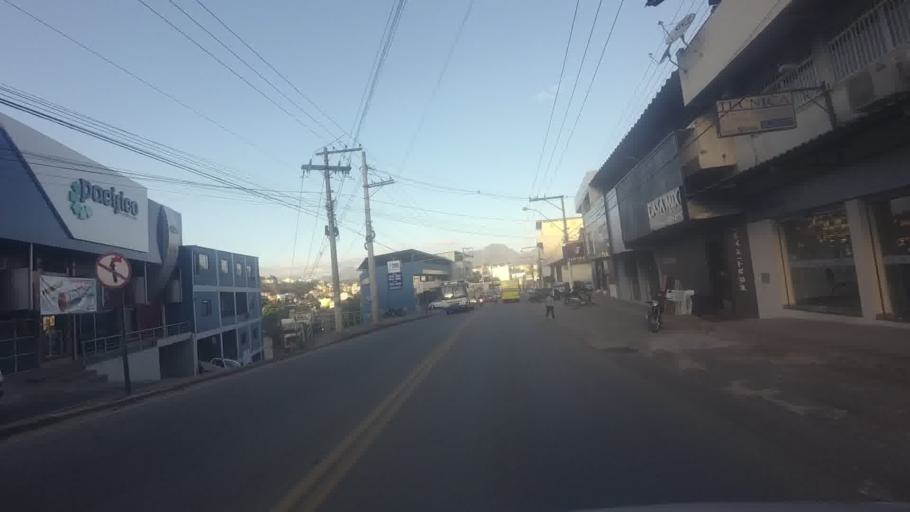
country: BR
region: Espirito Santo
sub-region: Cachoeiro De Itapemirim
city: Cachoeiro de Itapemirim
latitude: -20.8446
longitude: -41.1329
